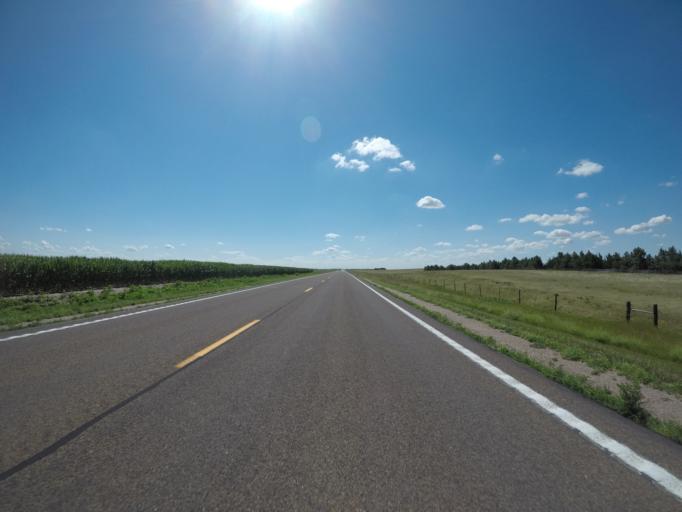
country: US
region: Nebraska
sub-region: Chase County
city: Imperial
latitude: 40.5376
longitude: -101.8603
